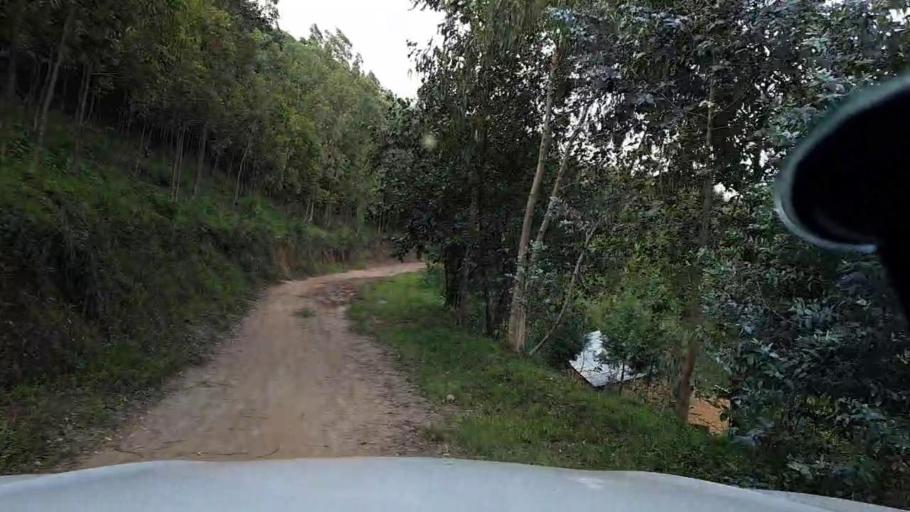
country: RW
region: Kigali
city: Kigali
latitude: -1.7844
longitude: 29.8337
